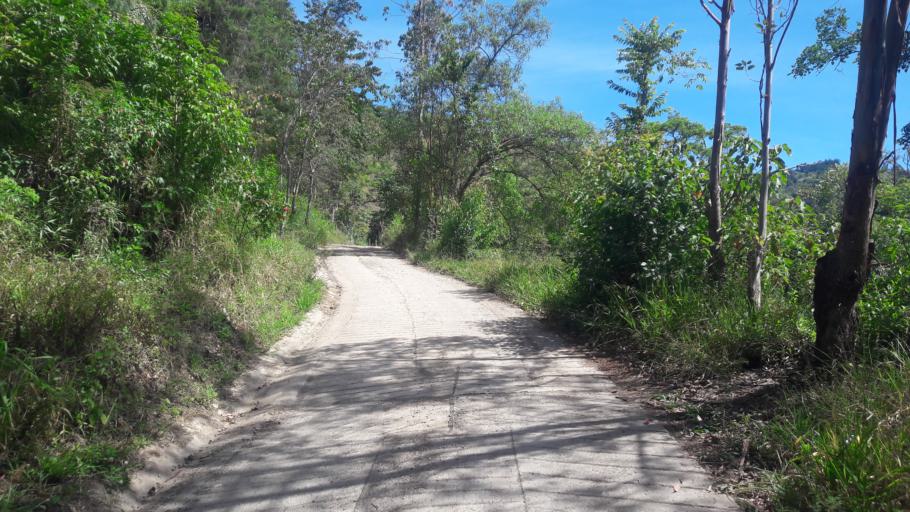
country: CO
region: Cundinamarca
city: Tenza
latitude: 5.0799
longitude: -73.4130
